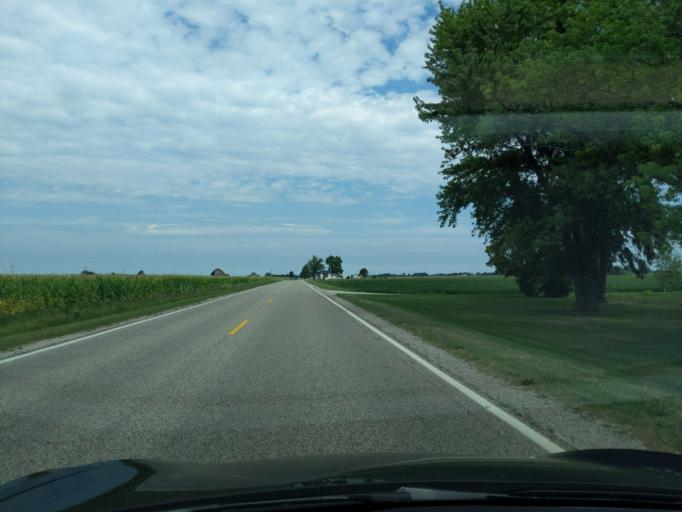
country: US
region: Michigan
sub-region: Gratiot County
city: Breckenridge
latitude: 43.3374
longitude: -84.4296
